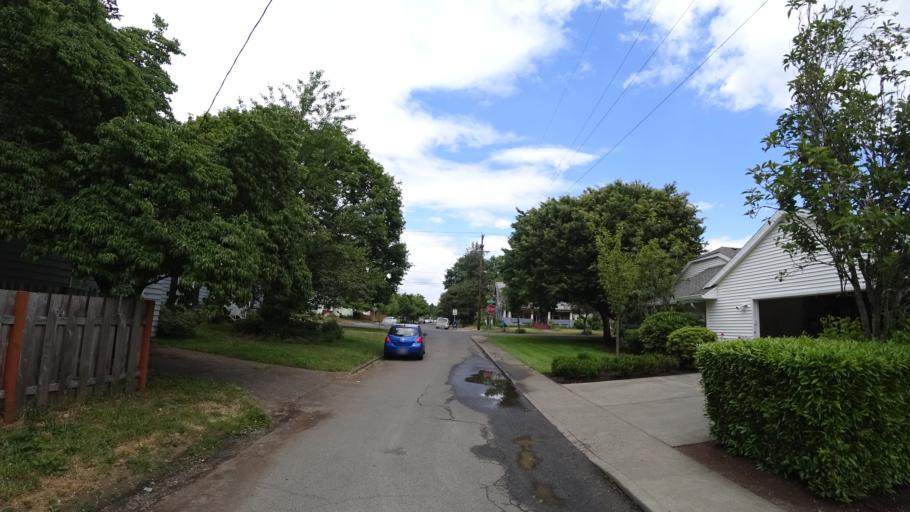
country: US
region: Oregon
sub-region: Washington County
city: West Haven
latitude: 45.5772
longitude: -122.7334
